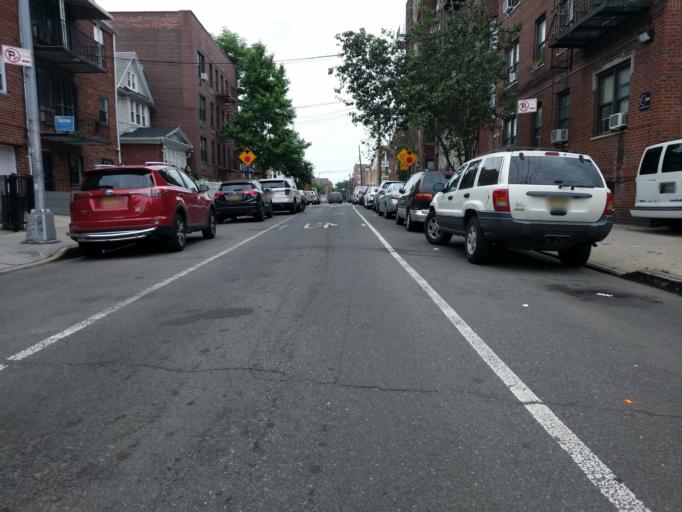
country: US
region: New York
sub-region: Queens County
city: Long Island City
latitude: 40.7457
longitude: -73.8817
